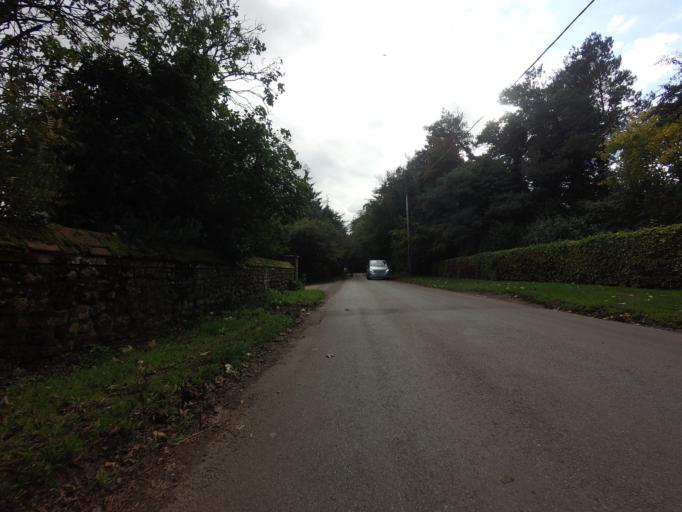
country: GB
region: England
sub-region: Norfolk
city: Snettisham
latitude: 52.8654
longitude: 0.5079
